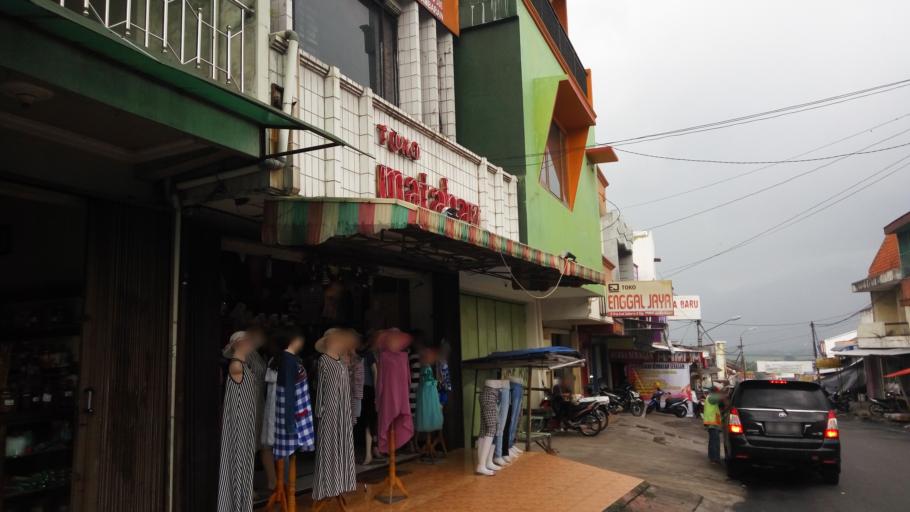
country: ID
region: Central Java
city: Ambarawa
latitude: -7.2575
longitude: 110.4058
